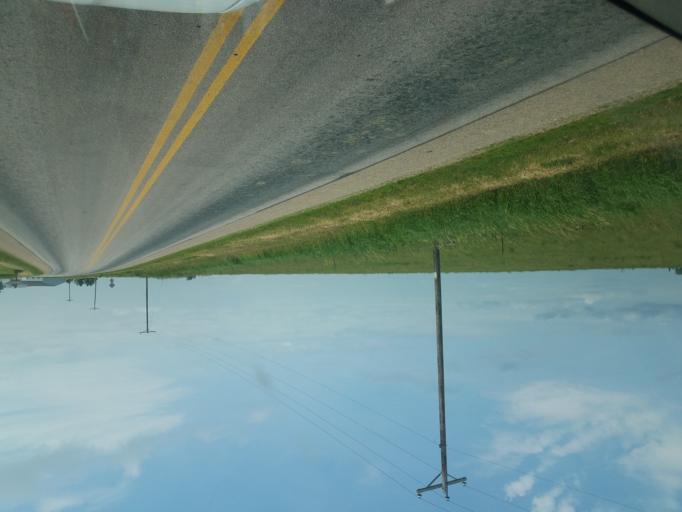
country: US
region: Wisconsin
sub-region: Monroe County
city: Cashton
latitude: 43.7564
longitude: -90.7479
